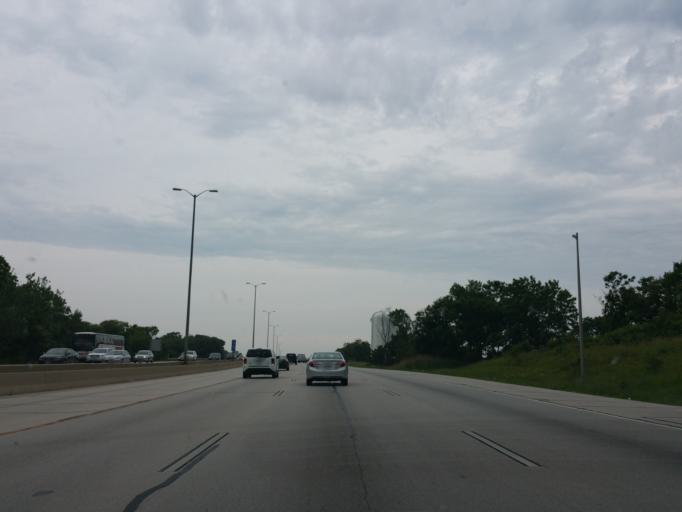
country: US
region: Wisconsin
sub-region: Waukesha County
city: Elm Grove
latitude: 43.0245
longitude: -88.0952
